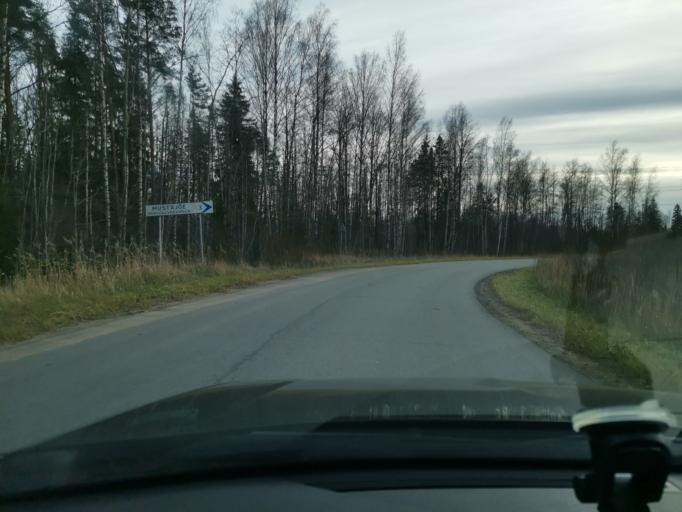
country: EE
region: Ida-Virumaa
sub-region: Sillamaee linn
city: Sillamae
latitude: 59.2707
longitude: 27.9138
